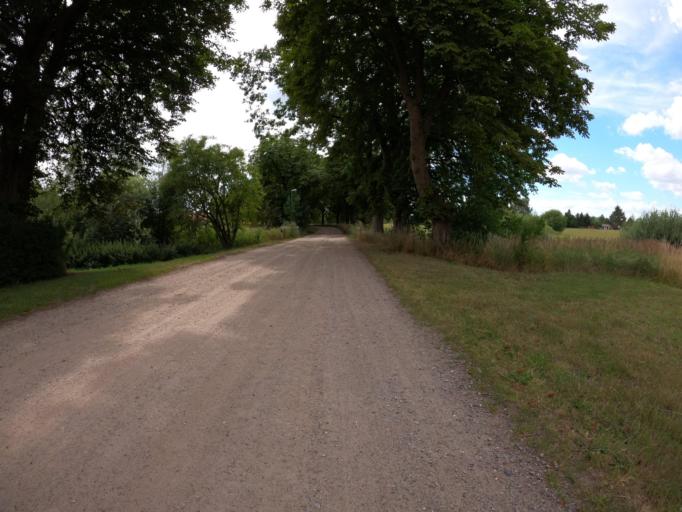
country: DE
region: Mecklenburg-Vorpommern
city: Loitz
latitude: 53.4008
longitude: 13.4457
